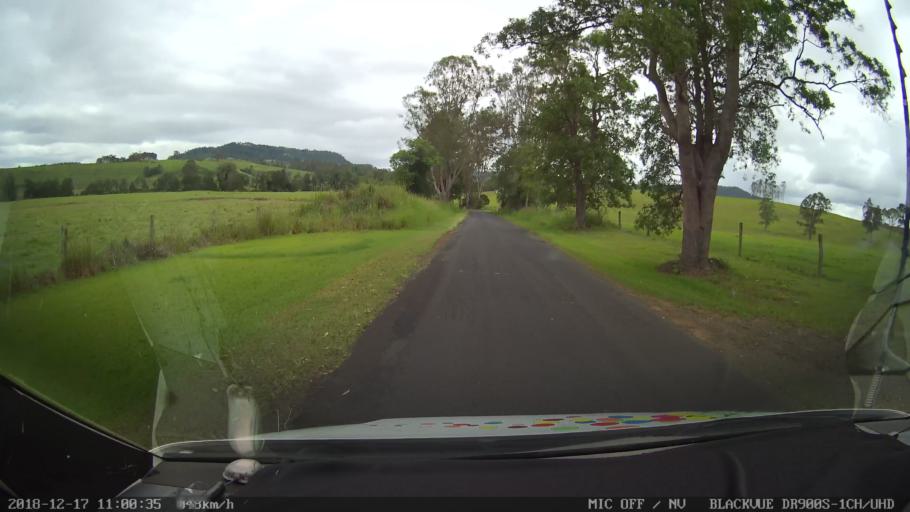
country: AU
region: New South Wales
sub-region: Richmond Valley
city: Casino
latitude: -28.8193
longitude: 152.6198
